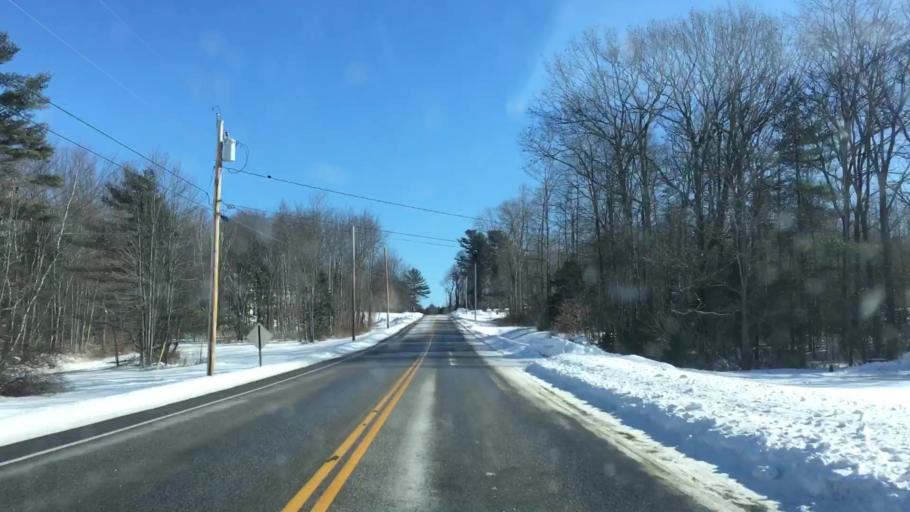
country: US
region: Maine
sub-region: Androscoggin County
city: Lisbon
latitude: 44.0286
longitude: -70.0807
